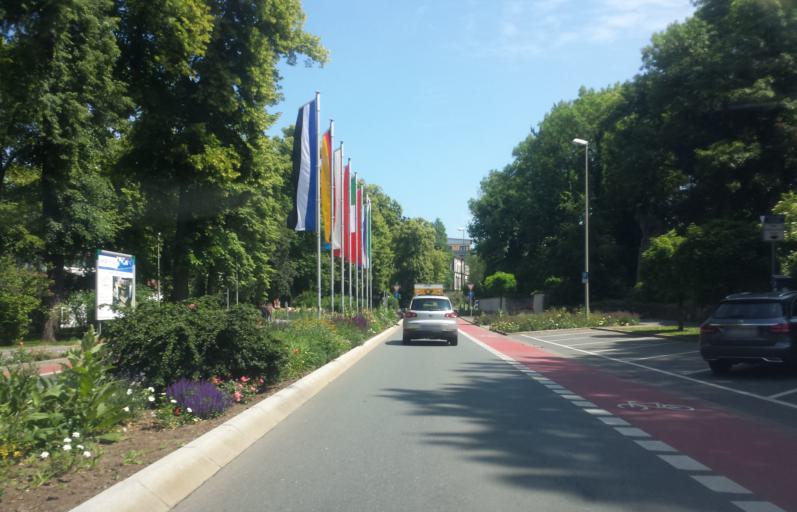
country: DE
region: Bavaria
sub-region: Upper Franconia
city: Kulmbach
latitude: 50.1049
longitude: 11.4482
